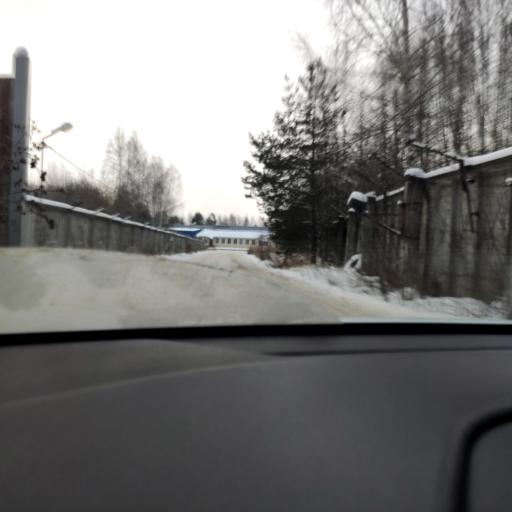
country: RU
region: Tatarstan
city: Osinovo
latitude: 55.8900
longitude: 48.8276
